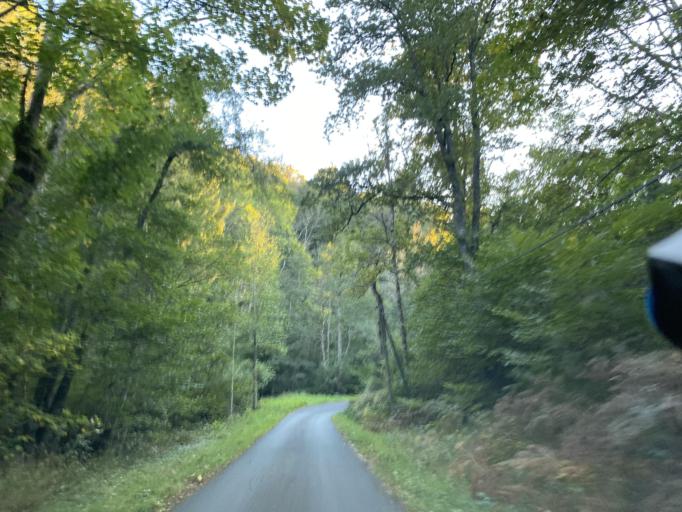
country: FR
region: Rhone-Alpes
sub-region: Departement de la Loire
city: Saint-Just-en-Chevalet
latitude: 45.9283
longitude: 3.8497
